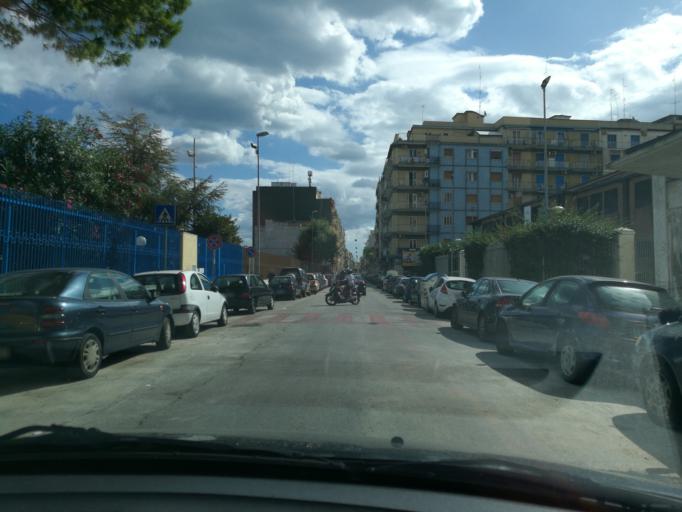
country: IT
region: Apulia
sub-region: Provincia di Bari
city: Bari
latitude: 41.1272
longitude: 16.8522
